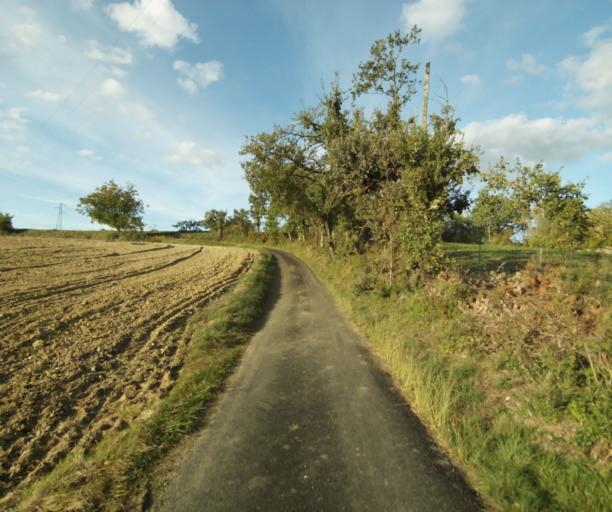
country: FR
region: Midi-Pyrenees
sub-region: Departement du Gers
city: Gondrin
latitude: 43.8869
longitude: 0.2693
